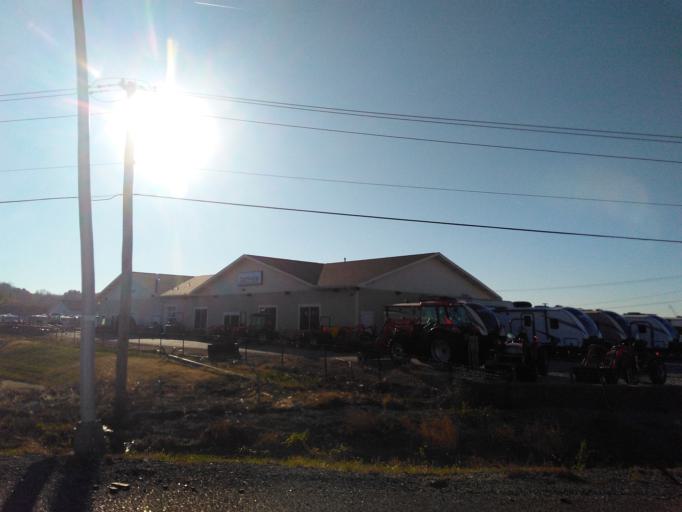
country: US
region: Illinois
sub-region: Madison County
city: Collinsville
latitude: 38.6751
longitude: -90.0209
